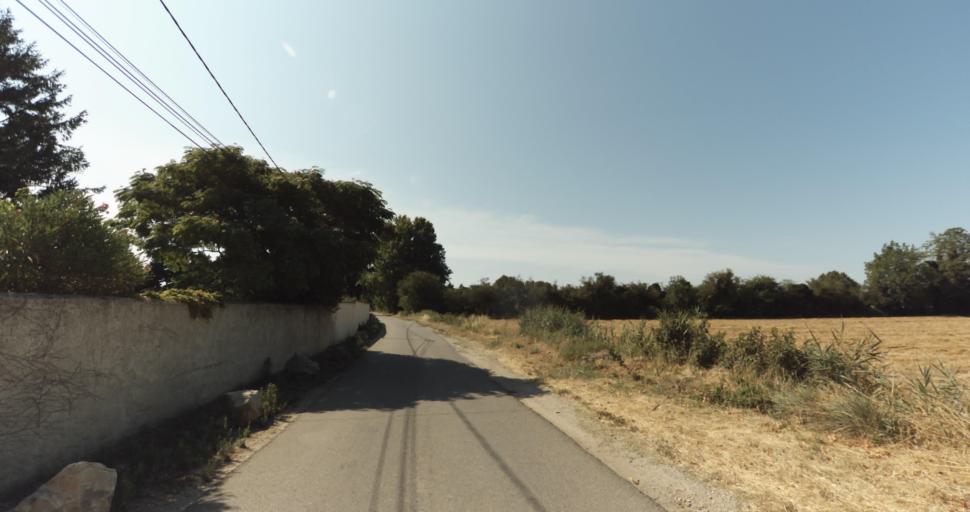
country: FR
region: Provence-Alpes-Cote d'Azur
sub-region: Departement du Vaucluse
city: Althen-des-Paluds
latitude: 44.0133
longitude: 4.9788
